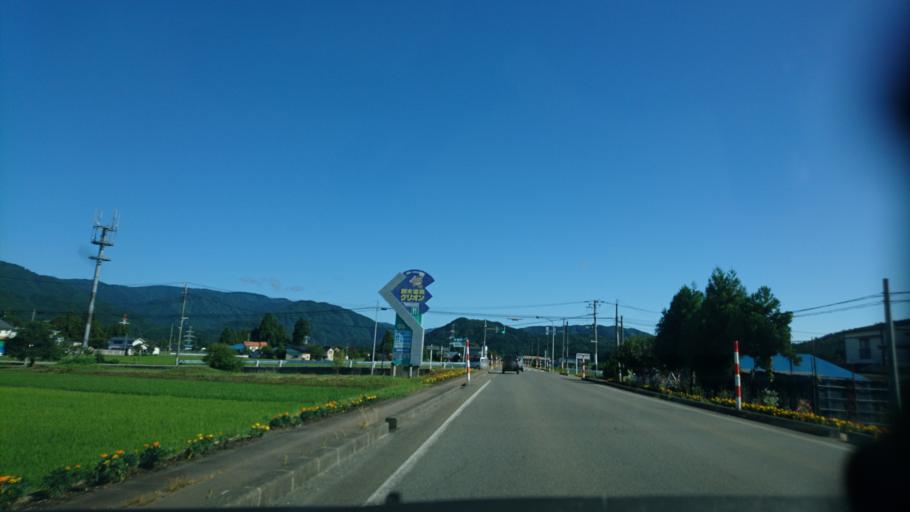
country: JP
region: Akita
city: Kakunodatemachi
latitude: 39.6590
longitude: 140.5701
